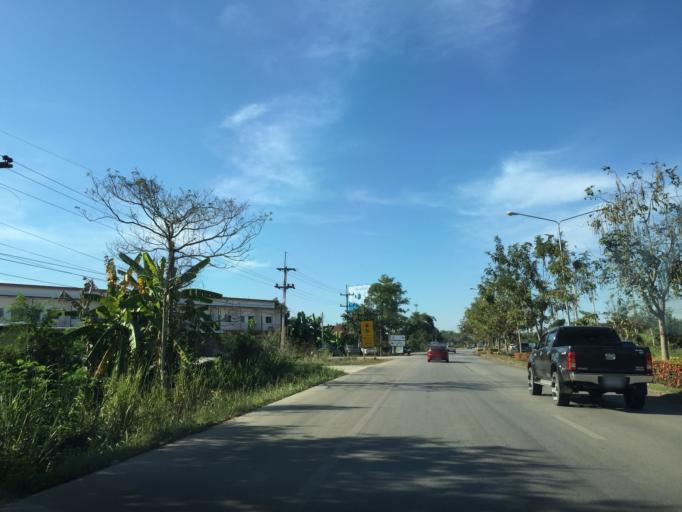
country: TH
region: Loei
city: Wang Saphung
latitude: 17.3214
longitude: 101.7626
